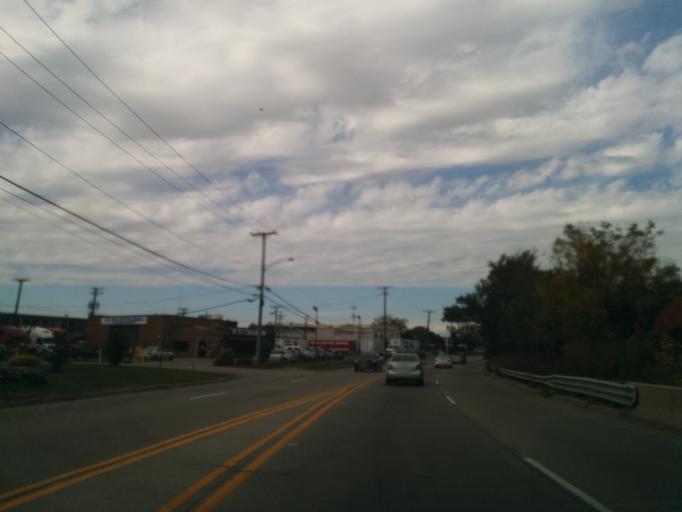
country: US
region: Illinois
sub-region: Cook County
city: Franklin Park
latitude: 41.9387
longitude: -87.8518
